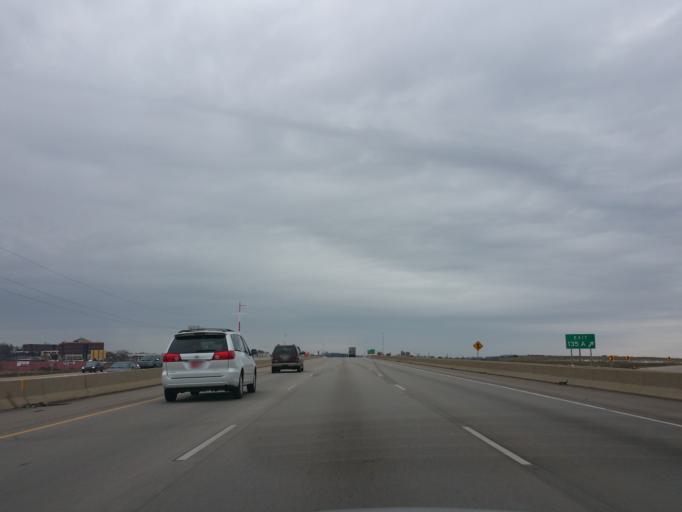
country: US
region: Wisconsin
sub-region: Dane County
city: Maple Bluff
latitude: 43.1405
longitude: -89.2984
